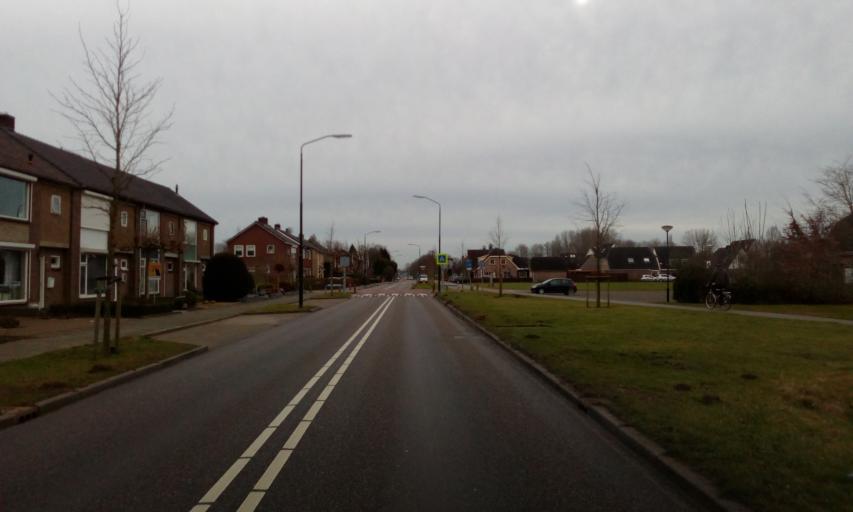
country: NL
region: North Brabant
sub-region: Gemeente Woudrichem
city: Woudrichem
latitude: 51.7917
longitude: 5.0281
